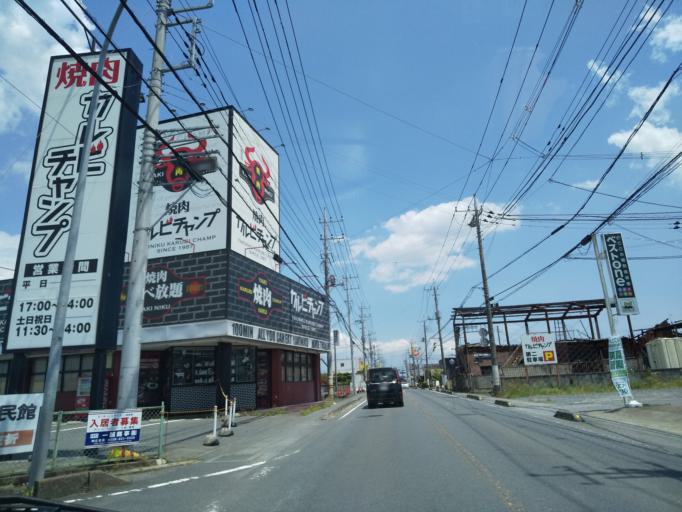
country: JP
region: Ibaraki
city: Ishioka
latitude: 36.1864
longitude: 140.2972
